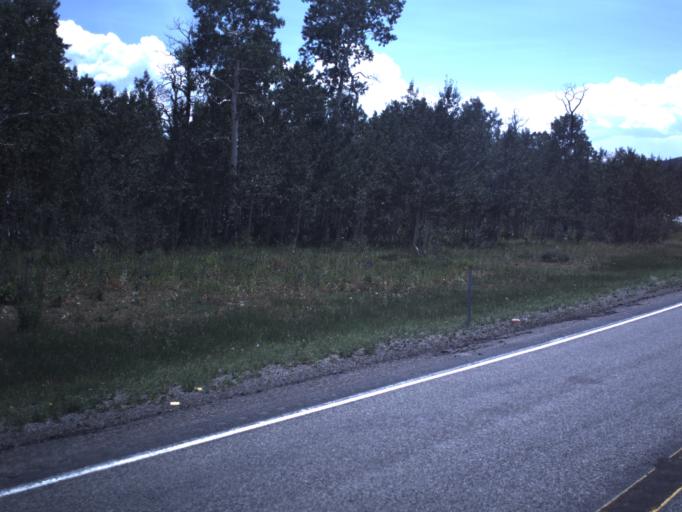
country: US
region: Utah
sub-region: Sanpete County
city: Fairview
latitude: 39.6553
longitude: -111.3302
